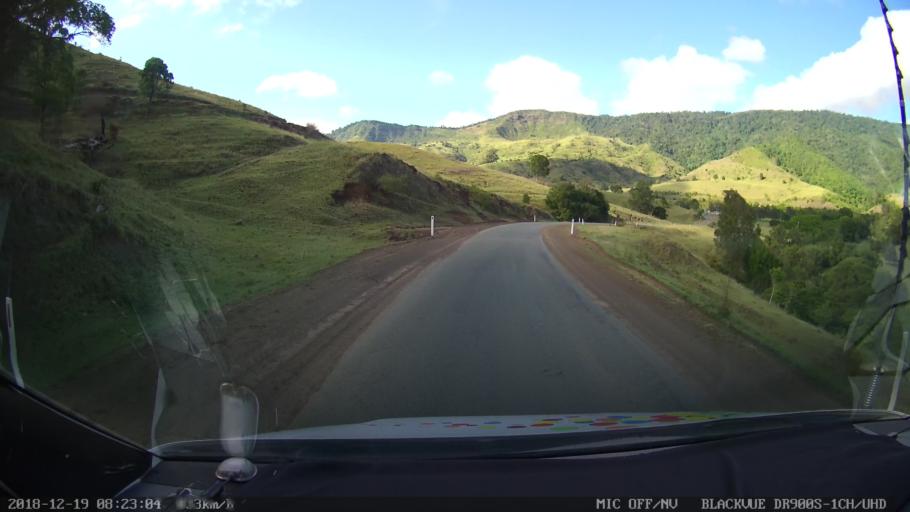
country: AU
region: New South Wales
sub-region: Kyogle
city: Kyogle
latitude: -28.3055
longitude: 152.9113
